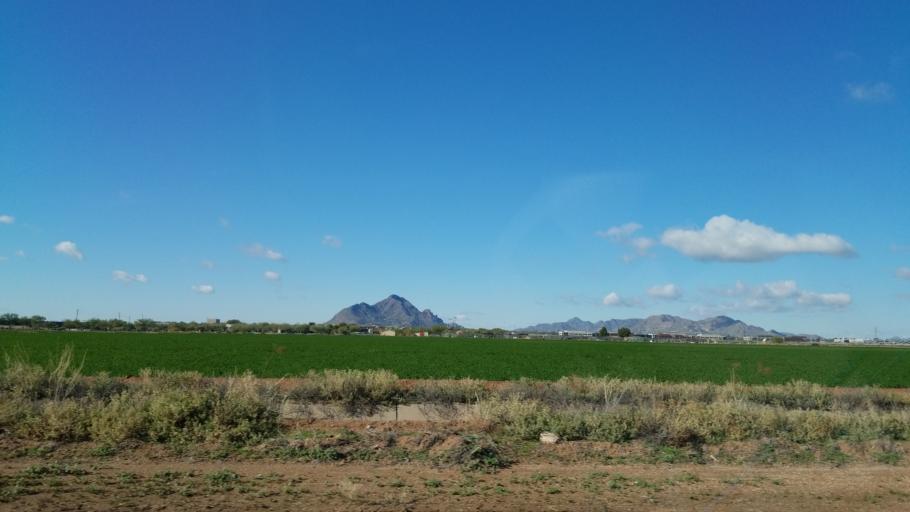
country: US
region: Arizona
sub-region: Maricopa County
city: Scottsdale
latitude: 33.5140
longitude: -111.8741
